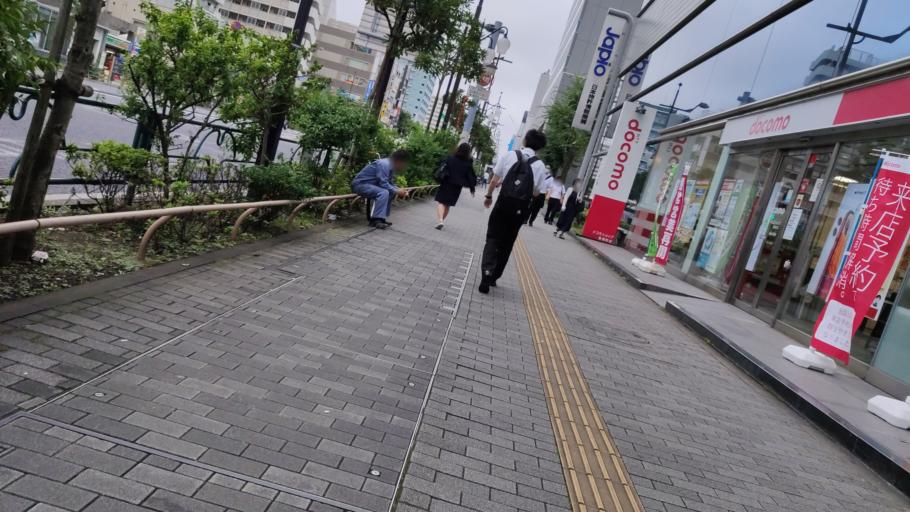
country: JP
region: Tokyo
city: Urayasu
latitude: 35.6695
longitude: 139.8174
